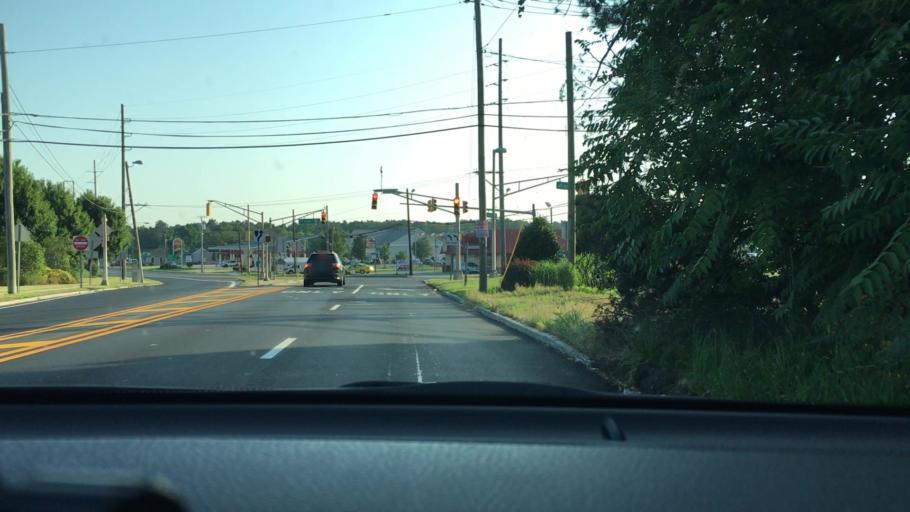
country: US
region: New Jersey
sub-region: Cumberland County
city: Millville
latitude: 39.4193
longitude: -75.0396
